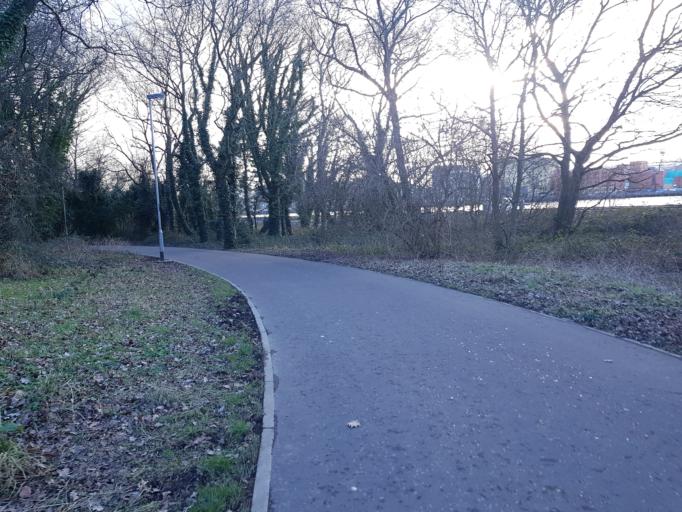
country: GB
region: Northern Ireland
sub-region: City of Derry
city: Derry
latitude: 55.0015
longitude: -7.3148
